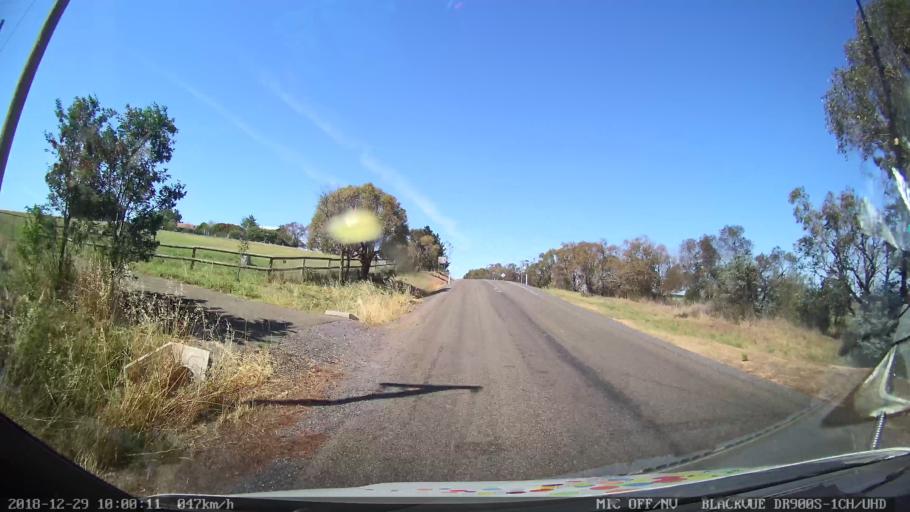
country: AU
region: New South Wales
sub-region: Goulburn Mulwaree
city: Goulburn
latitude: -34.7905
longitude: 149.4868
